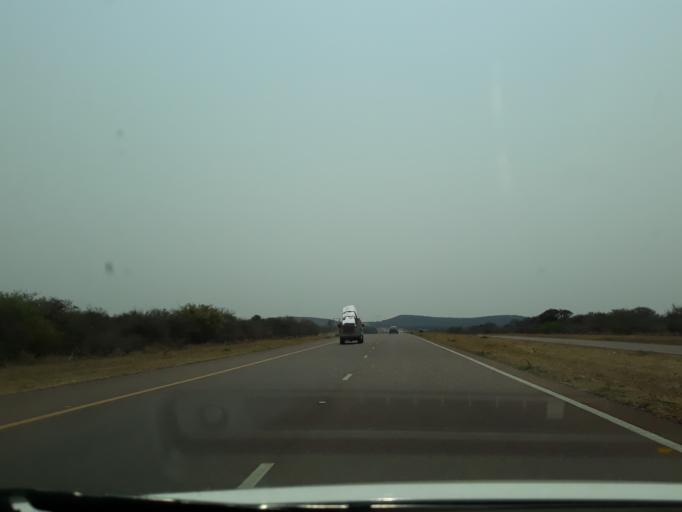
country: BW
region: Kgatleng
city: Bokaa
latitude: -24.4133
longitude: 26.0502
